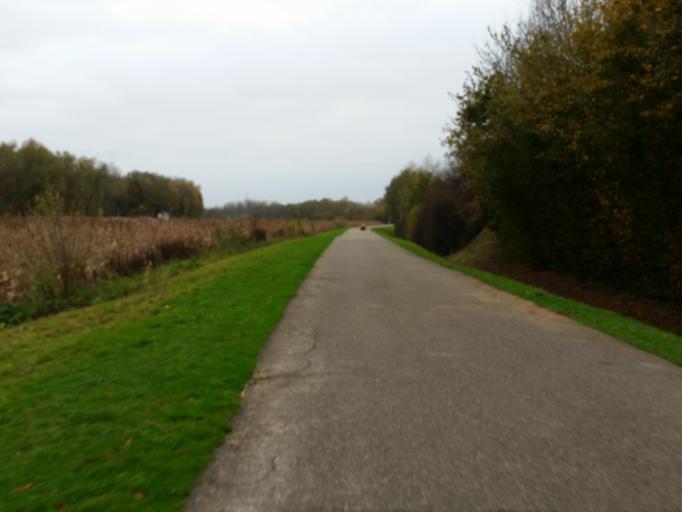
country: BE
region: Flanders
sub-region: Provincie Antwerpen
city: Duffel
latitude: 51.1097
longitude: 4.5297
